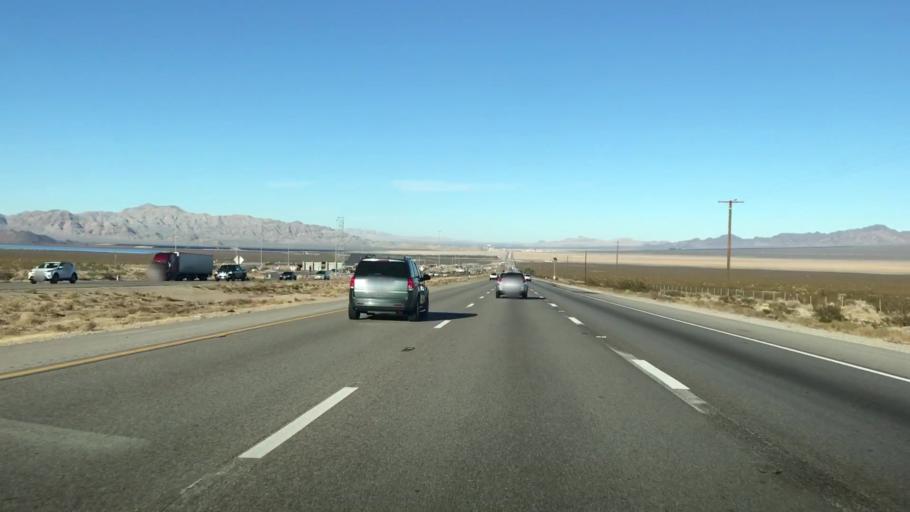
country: US
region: Nevada
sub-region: Clark County
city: Sandy Valley
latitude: 35.4969
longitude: -115.4383
